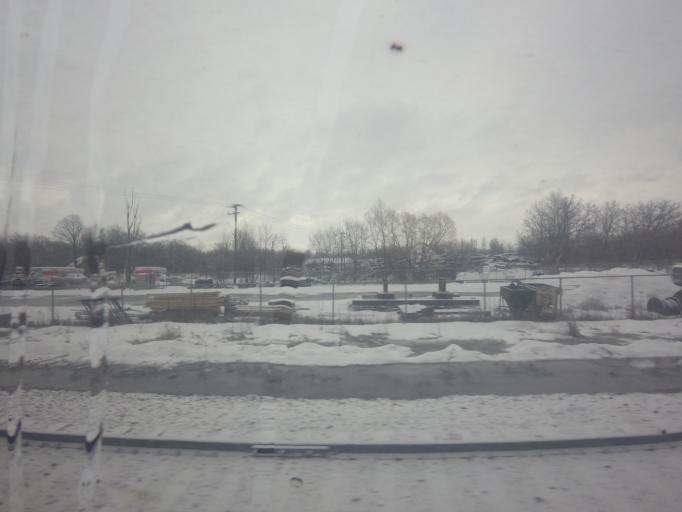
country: CA
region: Ontario
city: Bells Corners
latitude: 45.1872
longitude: -75.8230
